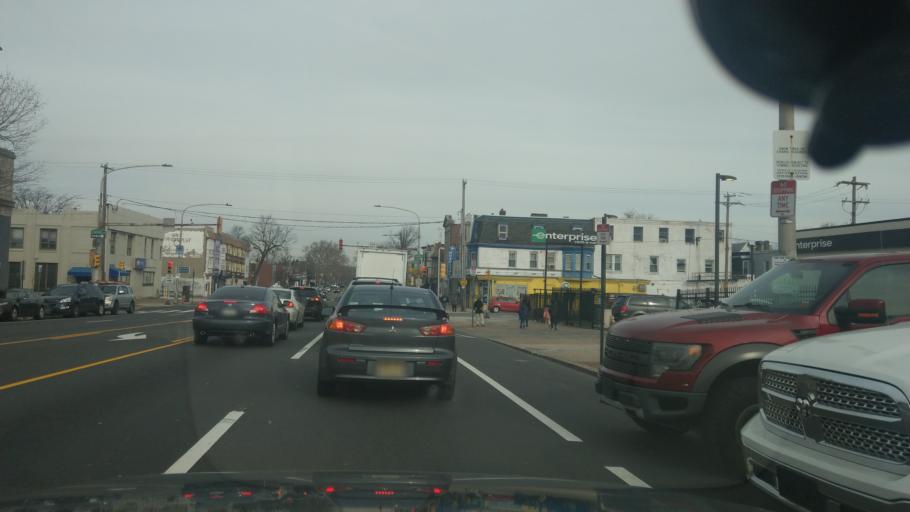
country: US
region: Pennsylvania
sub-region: Montgomery County
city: Wyncote
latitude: 40.0424
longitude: -75.1439
